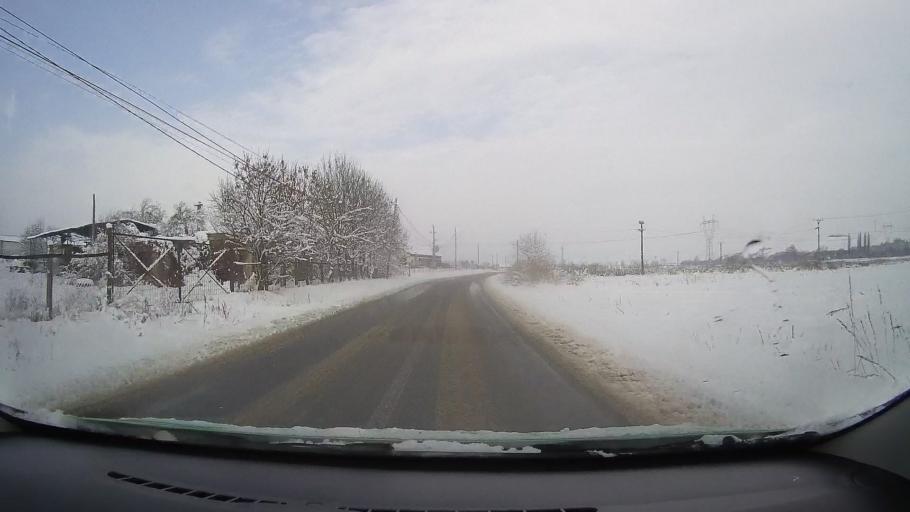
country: RO
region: Alba
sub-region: Comuna Pianu
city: Pianu de Jos
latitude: 45.9458
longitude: 23.4797
